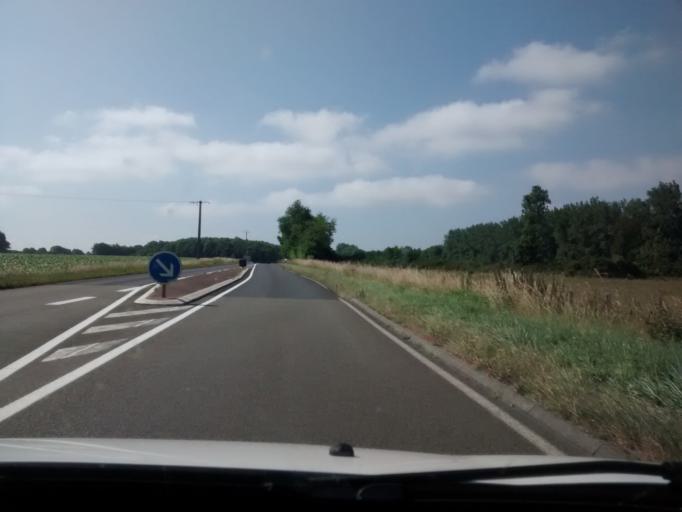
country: FR
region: Pays de la Loire
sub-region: Departement de la Sarthe
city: Vibraye
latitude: 48.1033
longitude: 0.7177
